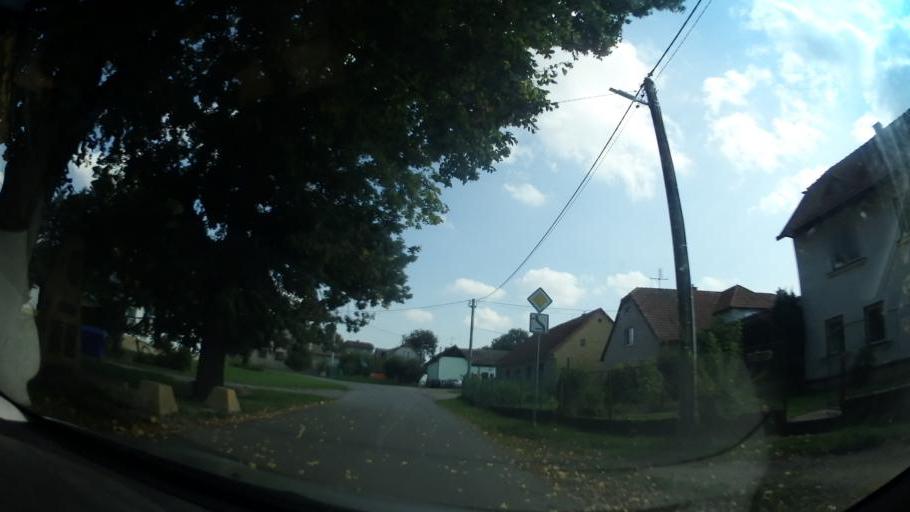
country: CZ
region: South Moravian
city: Olesnice
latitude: 49.5414
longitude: 16.3601
